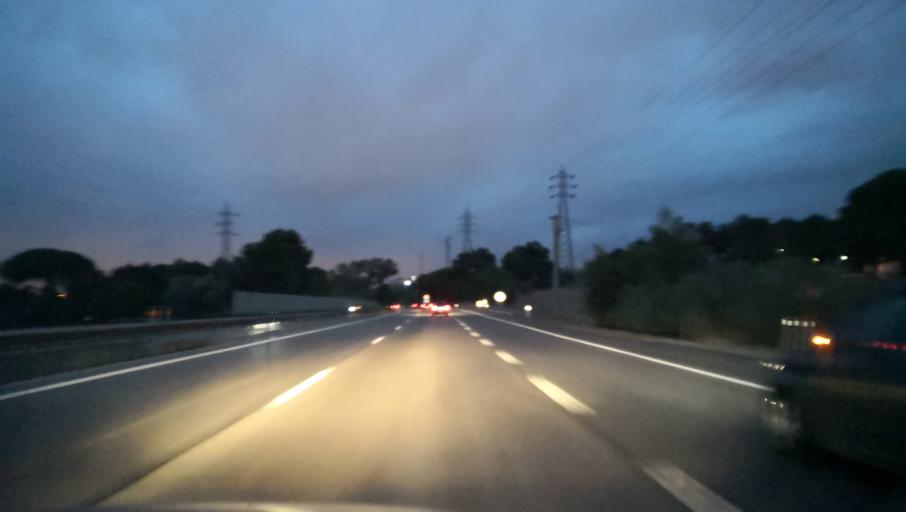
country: PT
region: Setubal
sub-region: Barreiro
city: Santo Antonio da Charneca
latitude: 38.6254
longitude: -9.0363
